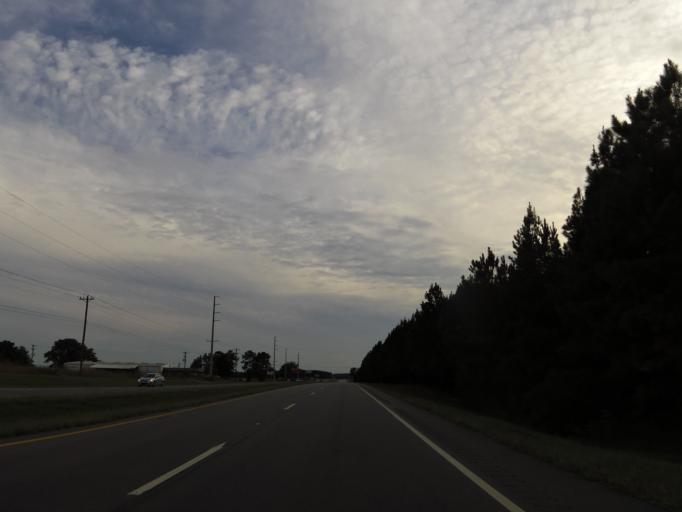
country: US
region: Alabama
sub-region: Escambia County
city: Atmore
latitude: 31.0742
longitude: -87.4850
